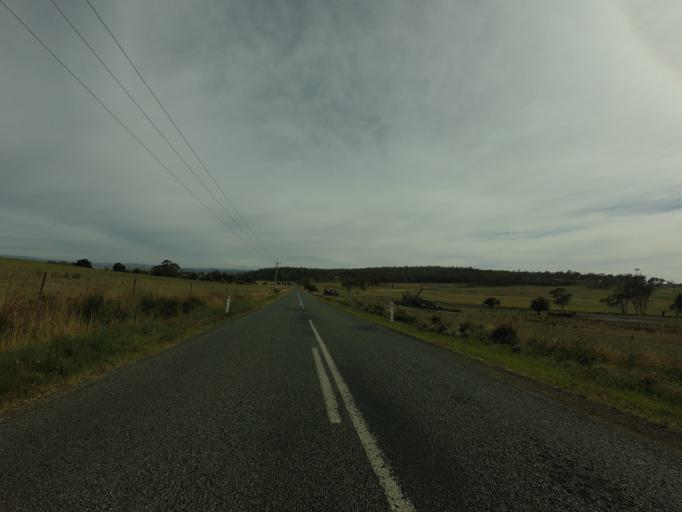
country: AU
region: Tasmania
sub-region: Brighton
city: Bridgewater
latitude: -42.3411
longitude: 147.4038
